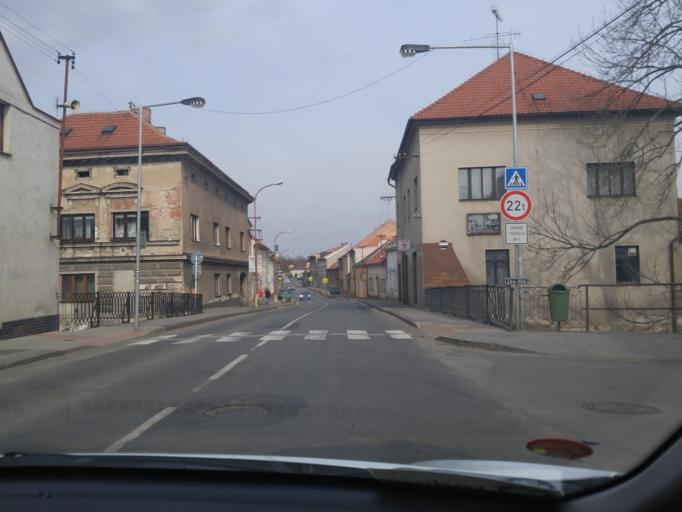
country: CZ
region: Central Bohemia
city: Kostelec nad Labem
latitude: 50.2277
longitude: 14.5872
